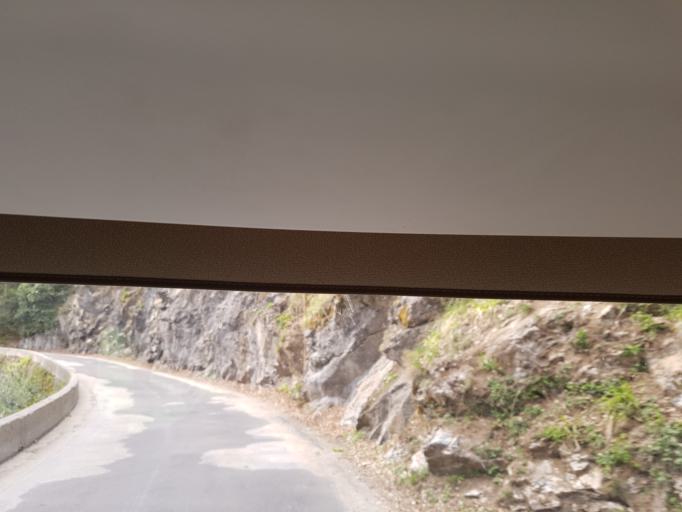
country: FR
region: Languedoc-Roussillon
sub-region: Departement de l'Aude
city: Quillan
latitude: 42.7707
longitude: 2.1190
